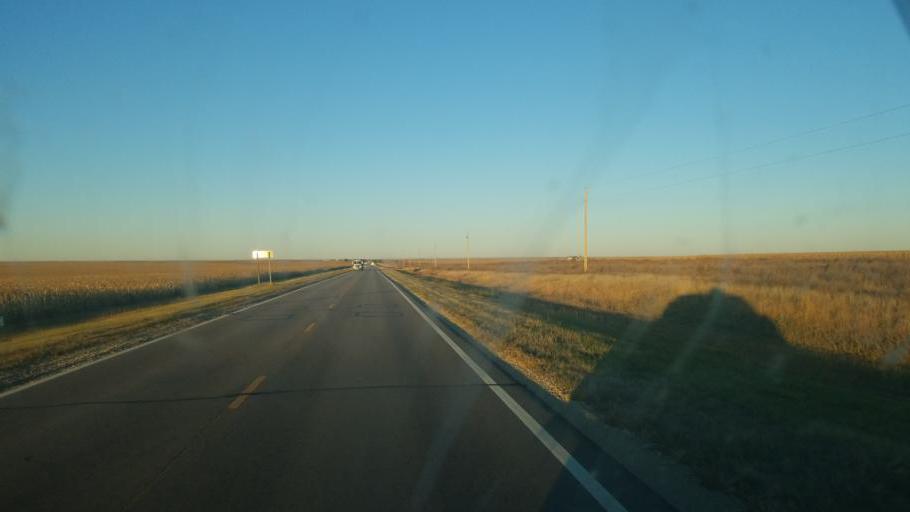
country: US
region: Kansas
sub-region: Wallace County
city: Sharon Springs
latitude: 38.8613
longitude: -102.0199
